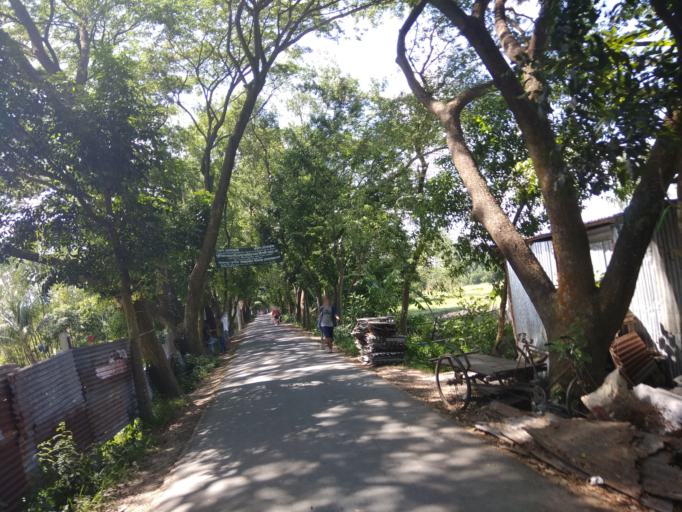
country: BD
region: Dhaka
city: Narayanganj
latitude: 23.4410
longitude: 90.4793
